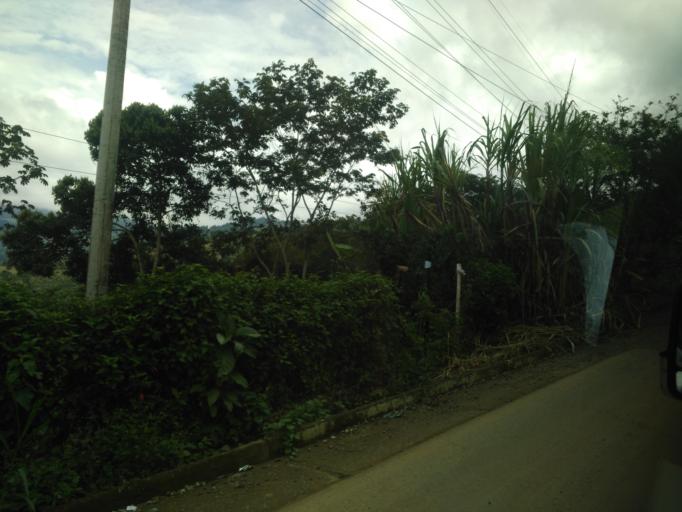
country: CO
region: Valle del Cauca
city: Sevilla
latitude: 4.2986
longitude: -75.8958
